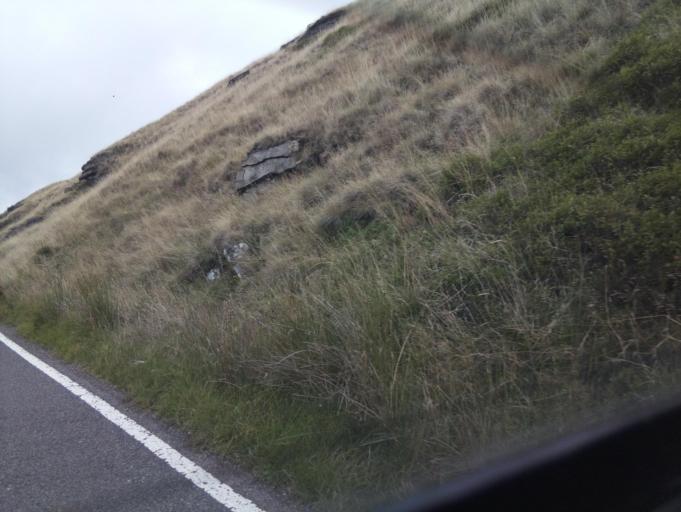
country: GB
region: England
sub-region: Kirklees
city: Meltham
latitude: 53.5267
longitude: -1.8566
